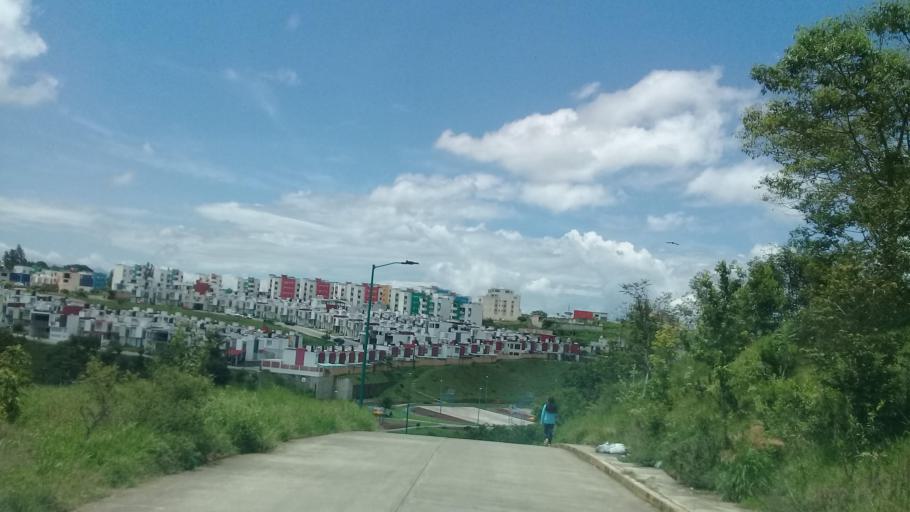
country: MX
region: Veracruz
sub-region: Xalapa
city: Fraccionamiento las Fuentes
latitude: 19.4974
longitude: -96.8829
